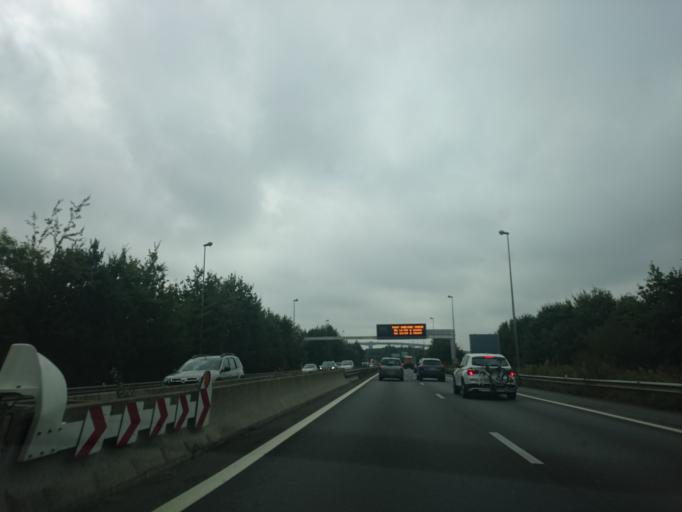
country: FR
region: Pays de la Loire
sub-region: Departement de la Loire-Atlantique
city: Saint-Herblain
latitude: 47.2053
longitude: -1.6242
